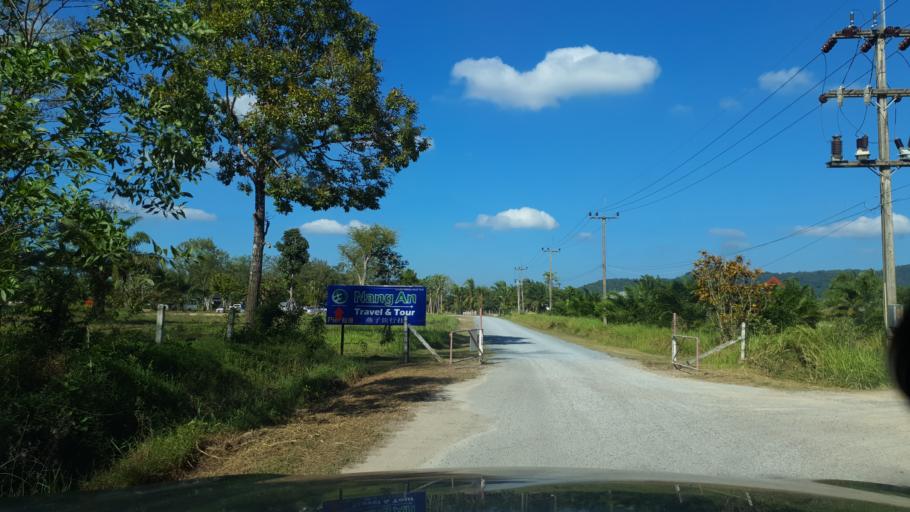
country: TH
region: Phangnga
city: Ban Ao Nang
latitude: 8.0495
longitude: 98.8017
